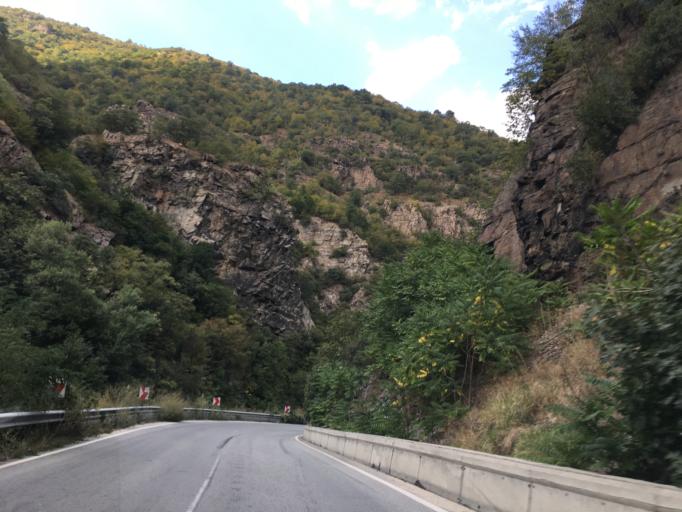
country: BG
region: Pazardzhik
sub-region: Obshtina Septemvri
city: Septemvri
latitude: 42.1370
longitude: 24.1252
